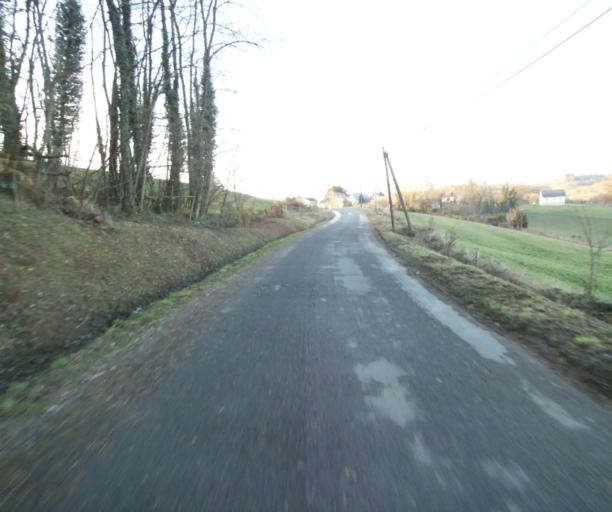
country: FR
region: Limousin
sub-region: Departement de la Correze
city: Laguenne
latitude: 45.2351
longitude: 1.8199
